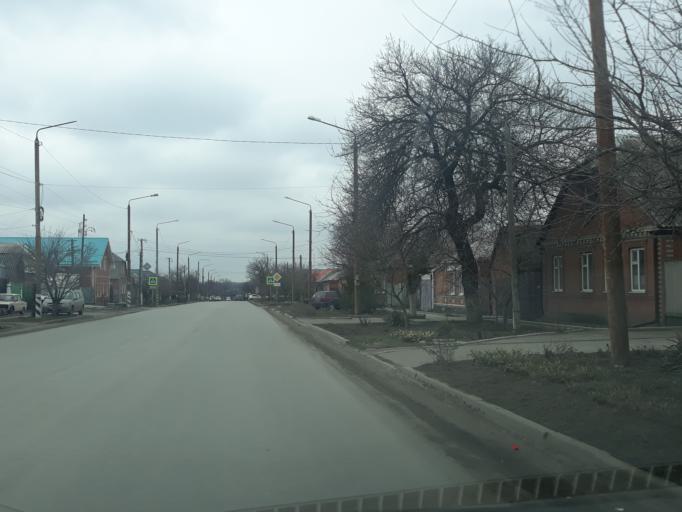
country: RU
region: Rostov
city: Taganrog
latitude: 47.2687
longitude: 38.8962
